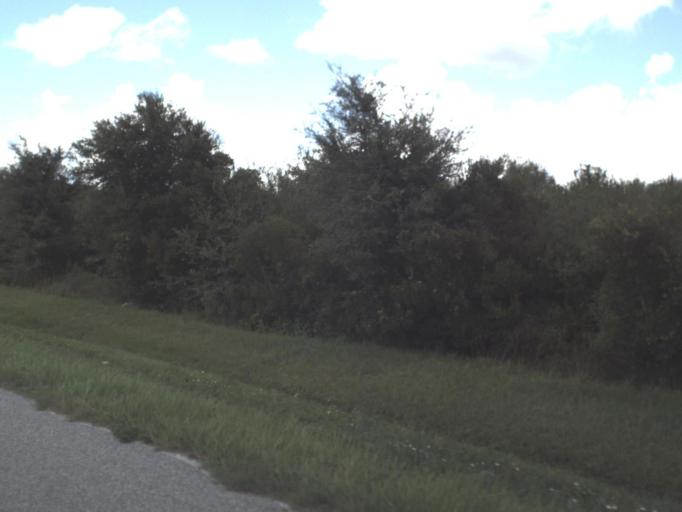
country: US
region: Florida
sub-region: Sarasota County
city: Lake Sarasota
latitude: 27.3523
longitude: -82.1689
